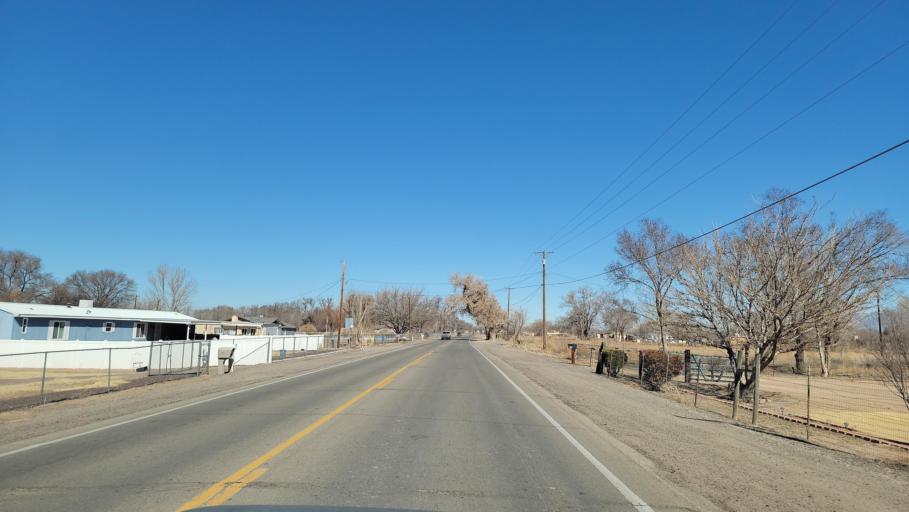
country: US
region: New Mexico
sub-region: Valencia County
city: Bosque Farms
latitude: 34.9185
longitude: -106.6930
